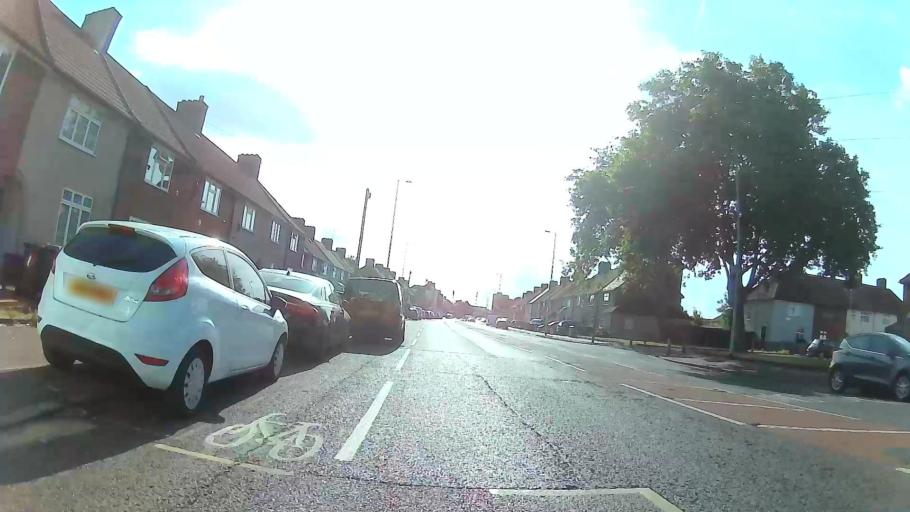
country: GB
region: England
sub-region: Greater London
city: Chadwell Heath
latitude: 51.5614
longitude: 0.1369
